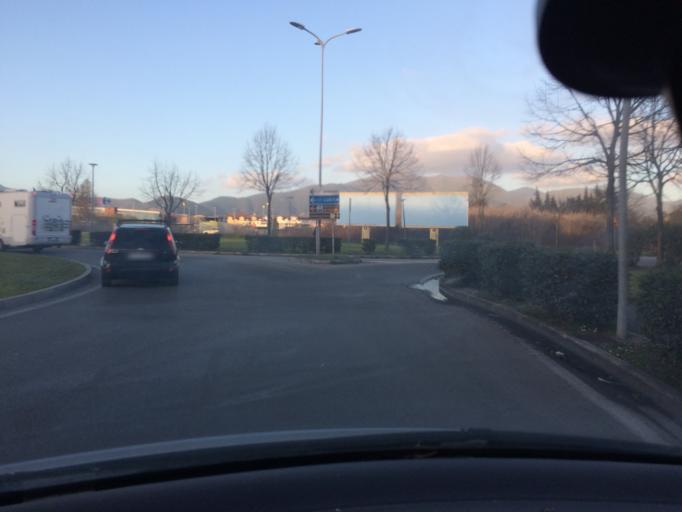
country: IT
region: Tuscany
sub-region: Province of Pisa
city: Pisa
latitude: 43.7227
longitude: 10.4158
